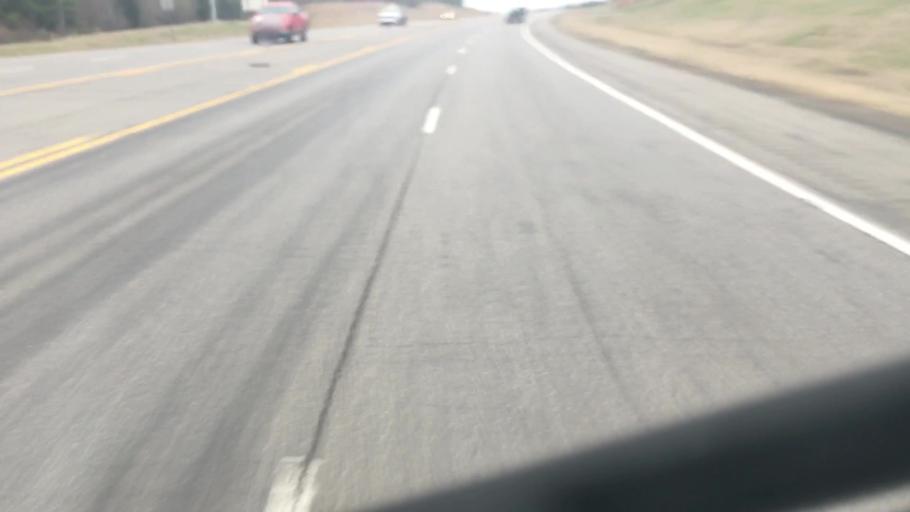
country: US
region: Alabama
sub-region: Walker County
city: Jasper
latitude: 33.7957
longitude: -87.2390
